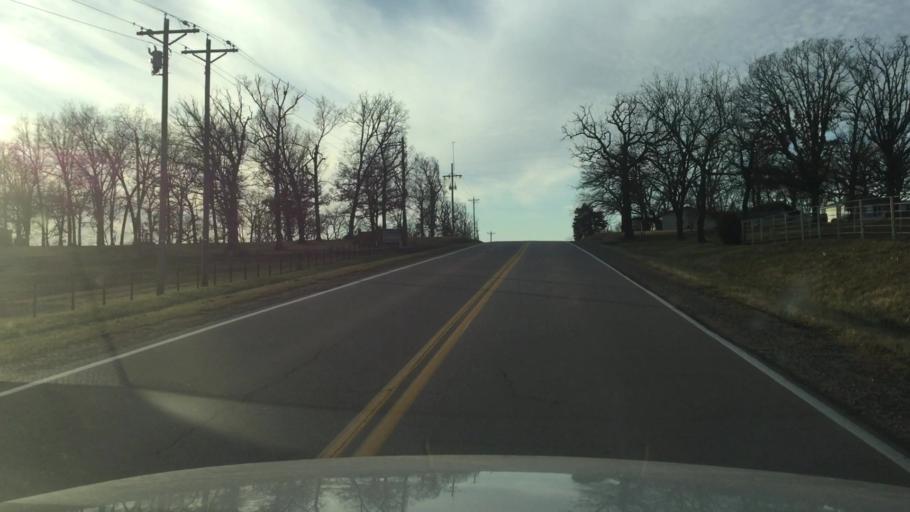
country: US
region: Missouri
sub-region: Miller County
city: Eldon
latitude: 38.3642
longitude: -92.5508
